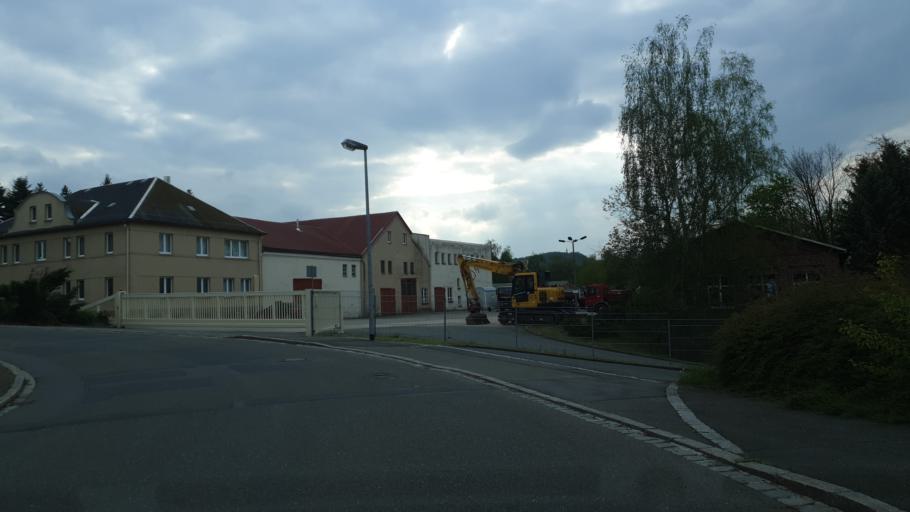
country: DE
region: Saxony
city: Oelsnitz
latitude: 50.7250
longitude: 12.7189
